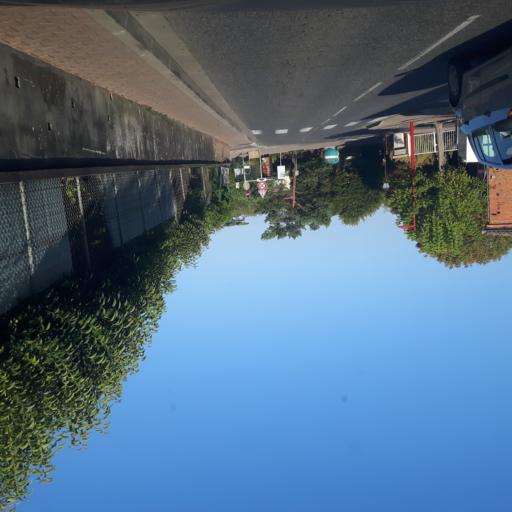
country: FR
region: Midi-Pyrenees
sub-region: Departement de la Haute-Garonne
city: Bouloc
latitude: 43.7805
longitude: 1.4061
